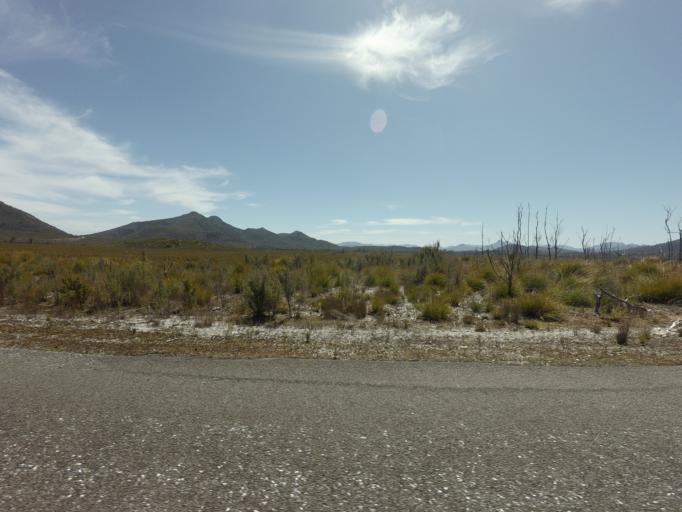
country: AU
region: Tasmania
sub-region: Huon Valley
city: Geeveston
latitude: -42.8623
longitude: 146.2057
